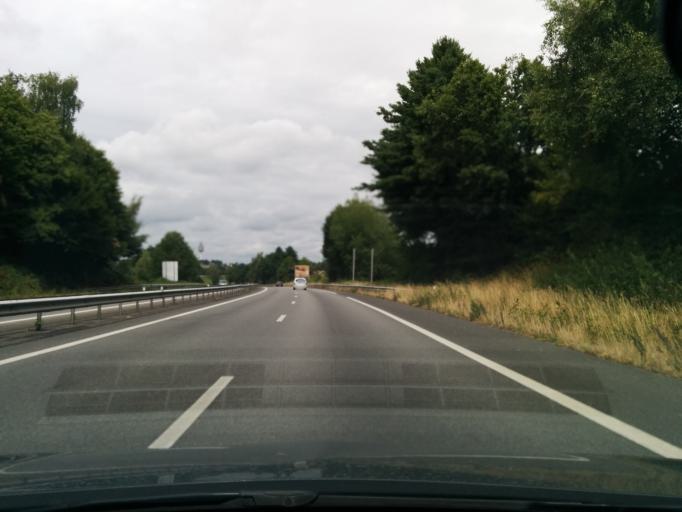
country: FR
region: Limousin
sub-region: Departement de la Haute-Vienne
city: Boisseuil
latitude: 45.7621
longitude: 1.3301
